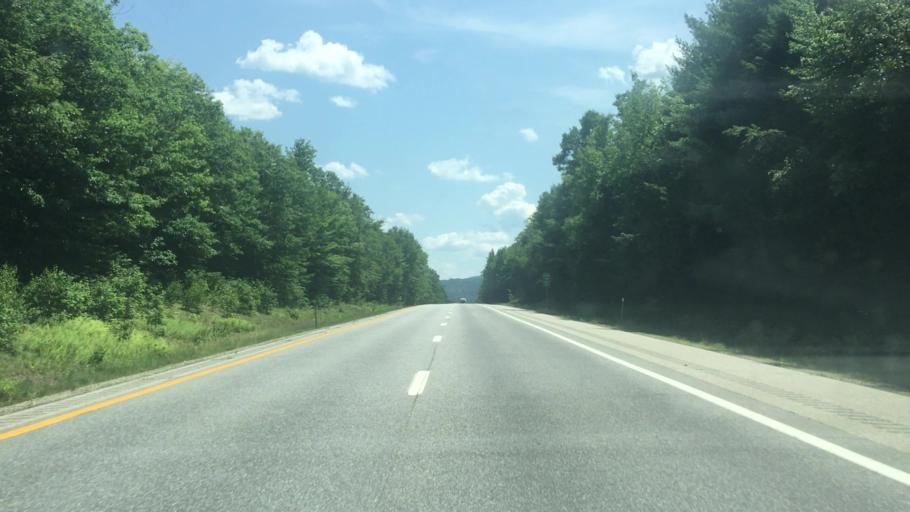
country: US
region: New Hampshire
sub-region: Merrimack County
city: Sutton
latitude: 43.3036
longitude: -71.8428
